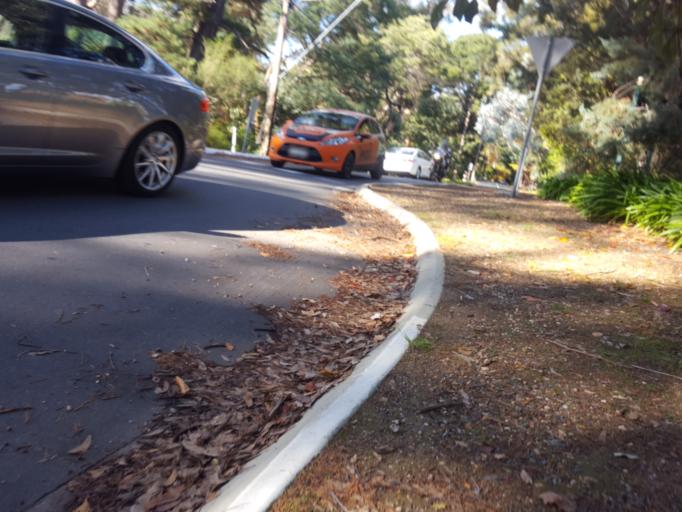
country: AU
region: South Australia
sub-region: Adelaide Hills
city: Crafers
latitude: -35.0032
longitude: 138.7079
